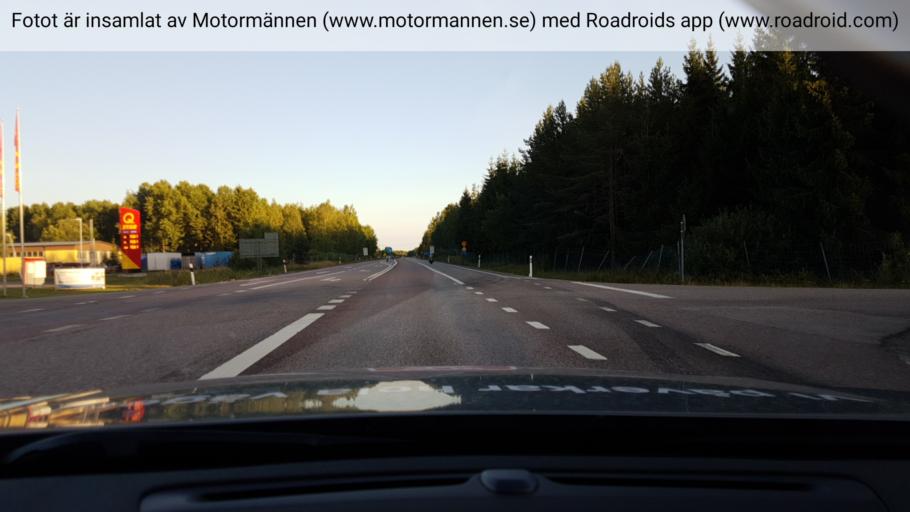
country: SE
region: Vaestmanland
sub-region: Surahammars Kommun
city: Ramnas
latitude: 59.8654
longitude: 16.0368
